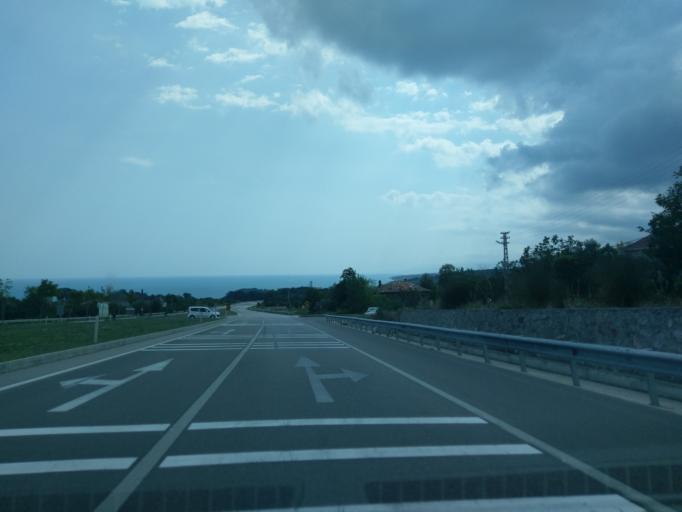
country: TR
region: Sinop
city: Kabali
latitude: 41.8475
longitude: 35.1305
